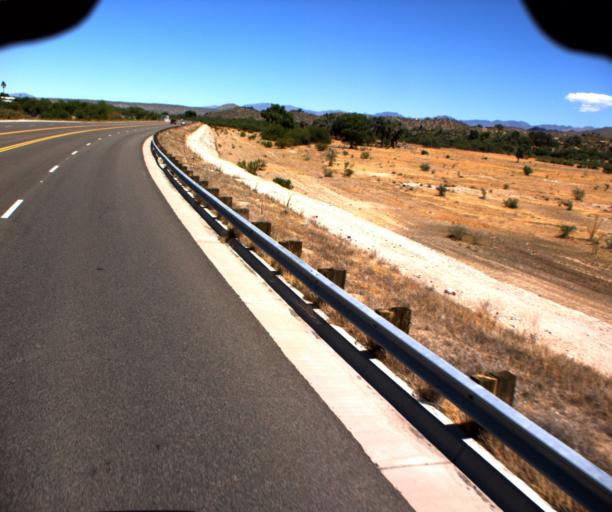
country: US
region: Arizona
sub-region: Maricopa County
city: Wickenburg
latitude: 33.9758
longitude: -112.7324
